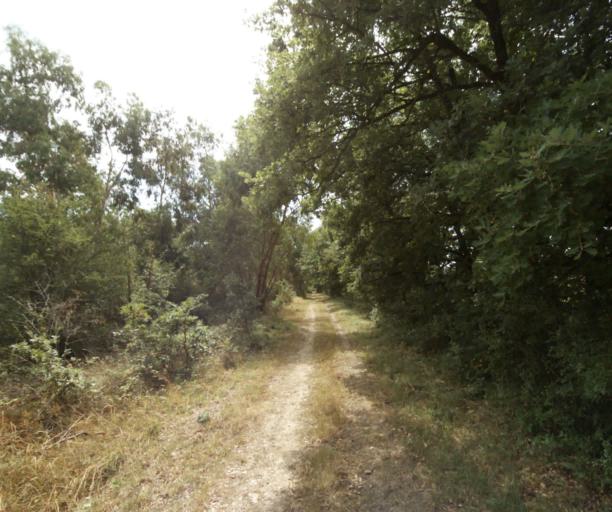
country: FR
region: Midi-Pyrenees
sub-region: Departement de la Haute-Garonne
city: Saint-Felix-Lauragais
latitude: 43.4234
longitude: 1.9309
